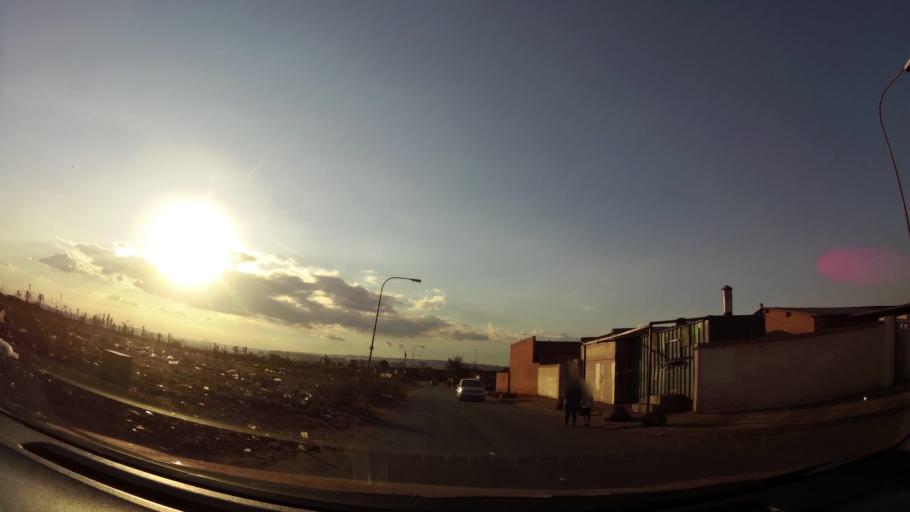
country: ZA
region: Gauteng
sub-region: City of Johannesburg Metropolitan Municipality
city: Soweto
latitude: -26.2260
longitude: 27.8550
